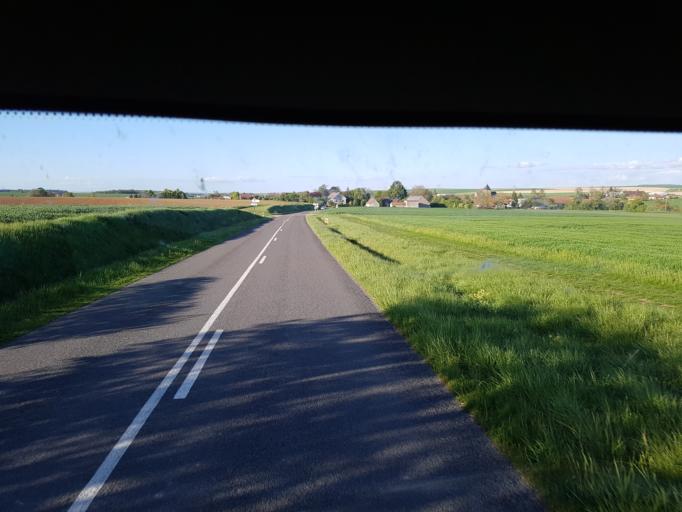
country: FR
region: Champagne-Ardenne
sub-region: Departement de l'Aube
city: Marigny-le-Chatel
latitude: 48.3844
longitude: 3.6481
